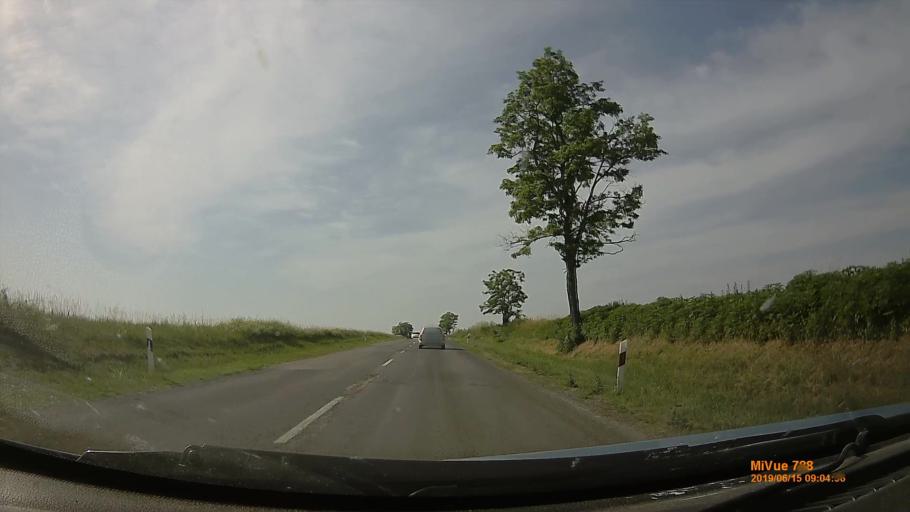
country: HU
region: Tolna
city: Iregszemcse
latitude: 46.7346
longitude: 18.1654
